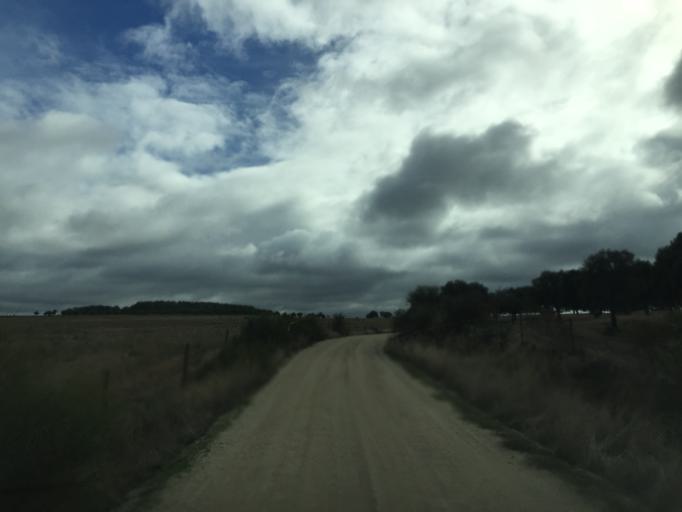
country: PT
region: Portalegre
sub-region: Alter do Chao
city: Alter do Chao
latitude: 39.2389
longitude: -7.6985
